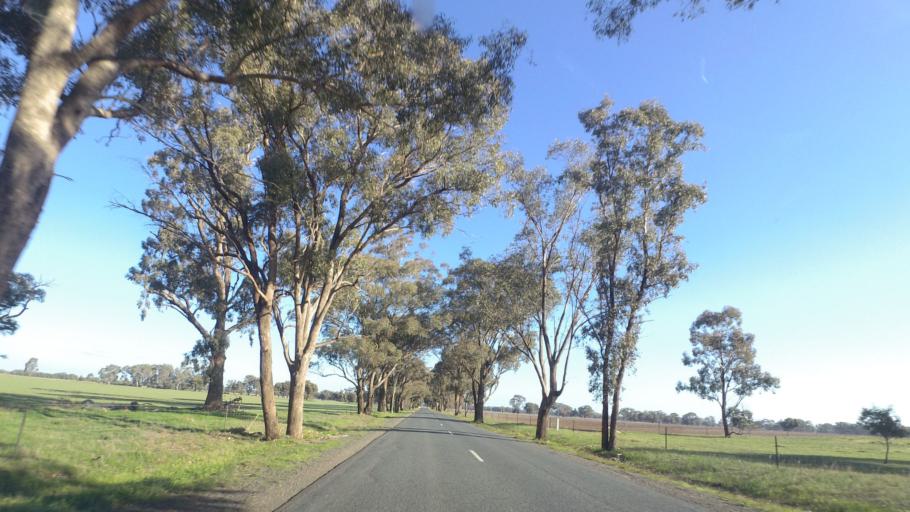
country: AU
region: Victoria
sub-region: Greater Bendigo
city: Epsom
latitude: -36.6334
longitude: 144.5283
